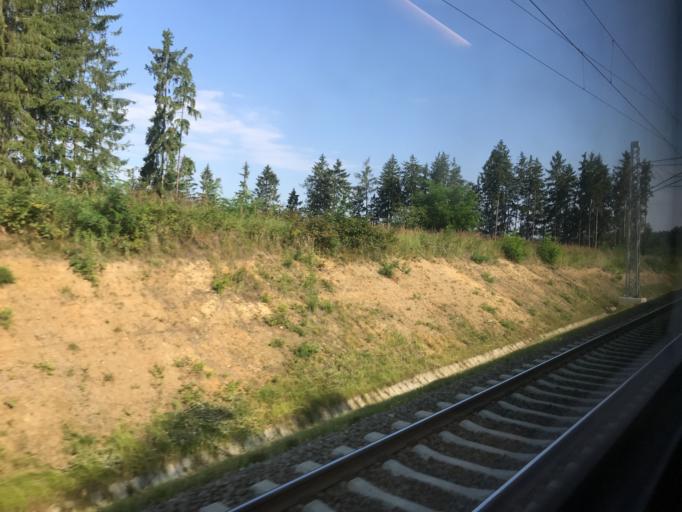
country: CZ
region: Jihocesky
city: Chotoviny
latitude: 49.4427
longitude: 14.6907
